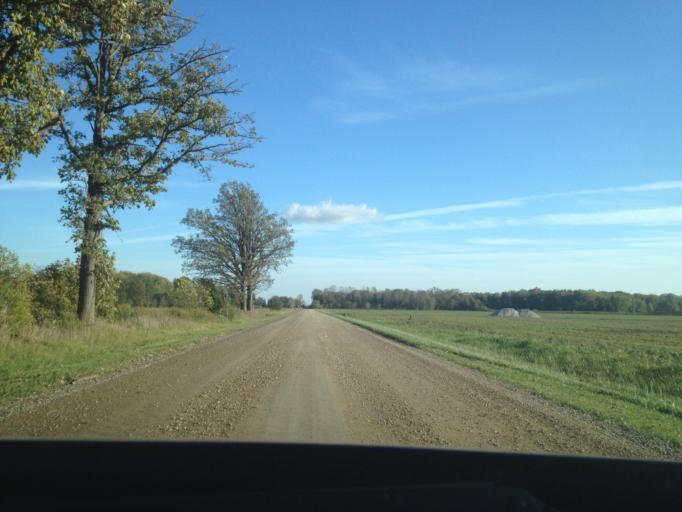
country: CA
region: Ontario
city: Delaware
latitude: 42.6616
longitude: -81.5602
